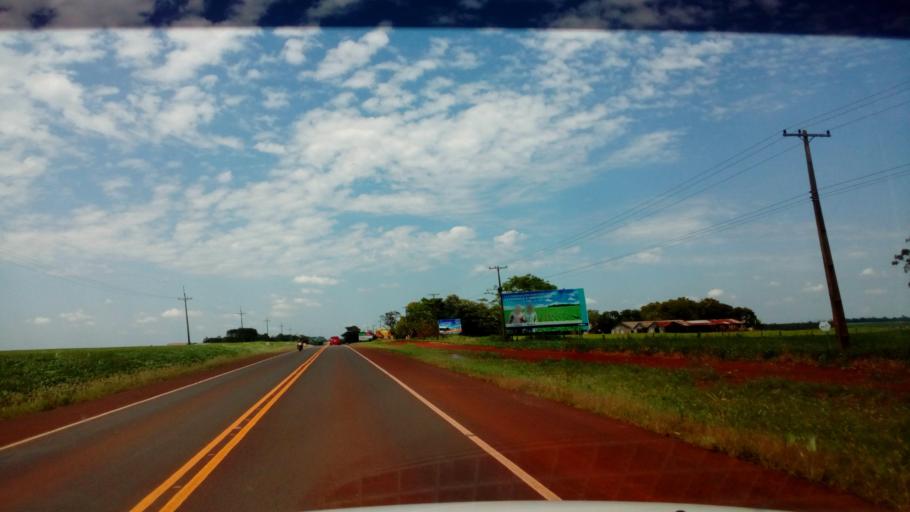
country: PY
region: Alto Parana
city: Santa Rita
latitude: -25.7295
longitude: -55.0412
